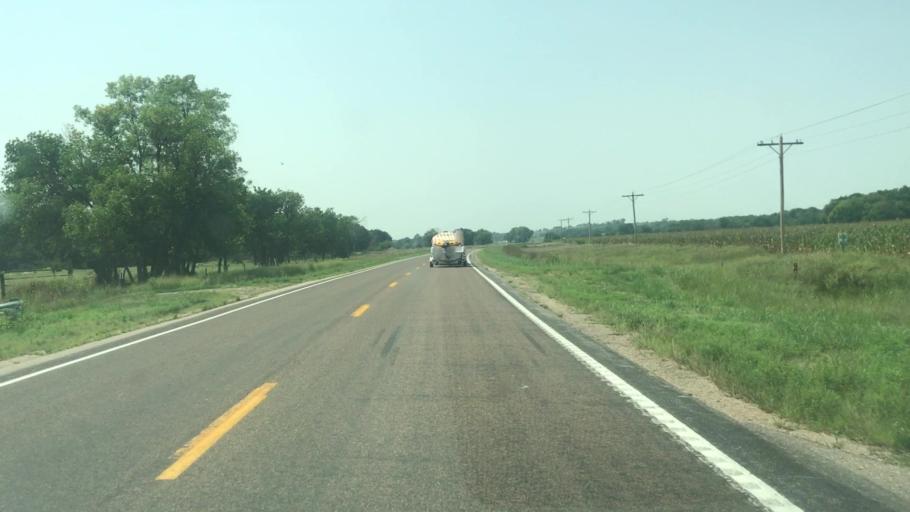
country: US
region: Nebraska
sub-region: Buffalo County
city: Ravenna
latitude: 41.0760
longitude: -98.6836
